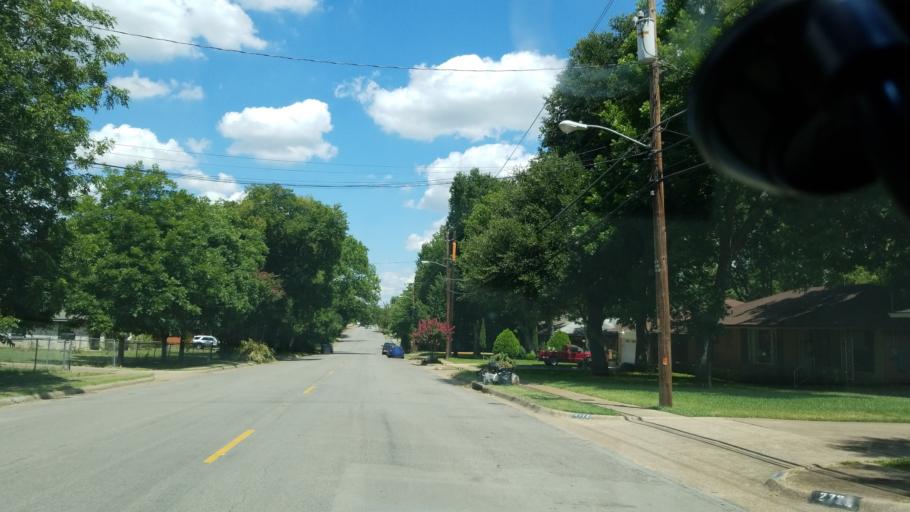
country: US
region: Texas
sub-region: Dallas County
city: Cockrell Hill
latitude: 32.6982
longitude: -96.8649
